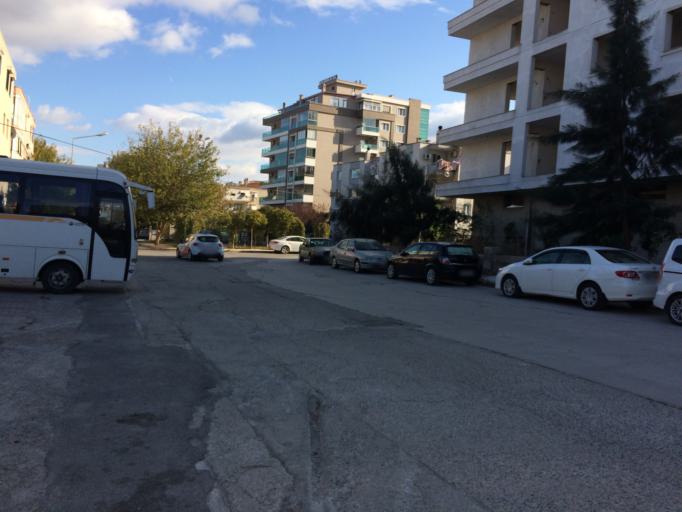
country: TR
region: Izmir
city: Karsiyaka
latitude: 38.4903
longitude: 27.0612
